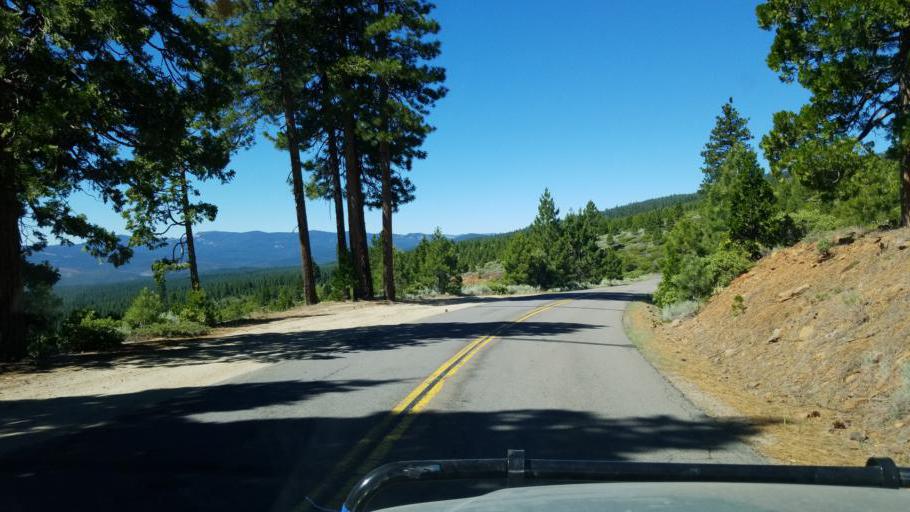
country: US
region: California
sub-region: Lassen County
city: Susanville
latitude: 40.4786
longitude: -120.7479
